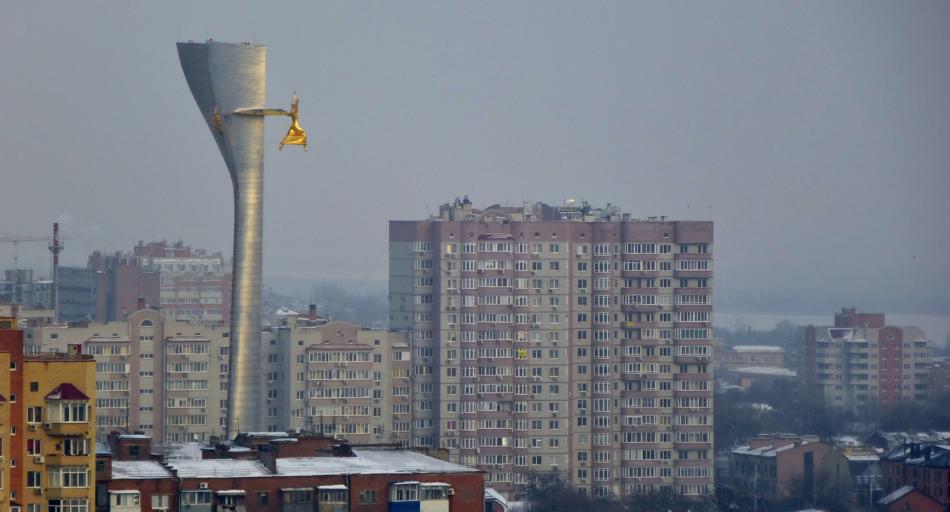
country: RU
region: Rostov
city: Rostov-na-Donu
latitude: 47.2265
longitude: 39.7421
